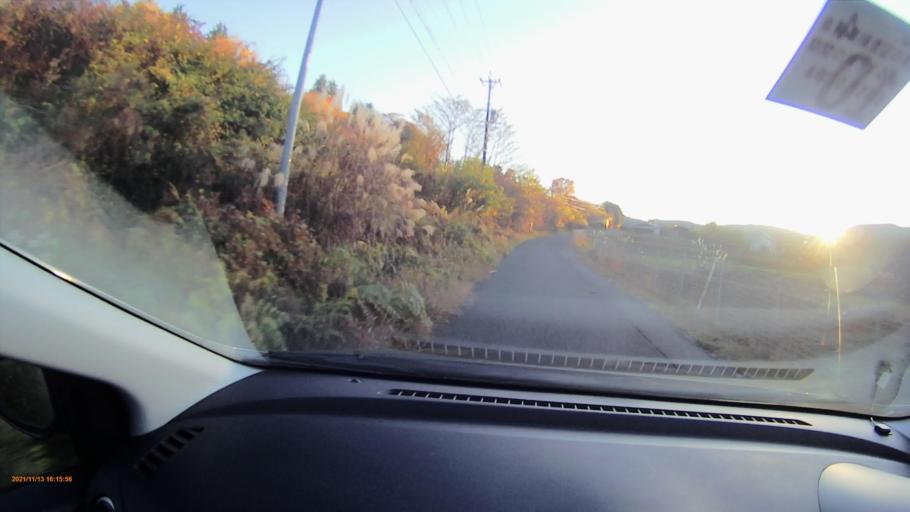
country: JP
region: Gifu
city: Nakatsugawa
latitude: 35.5783
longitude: 137.5104
